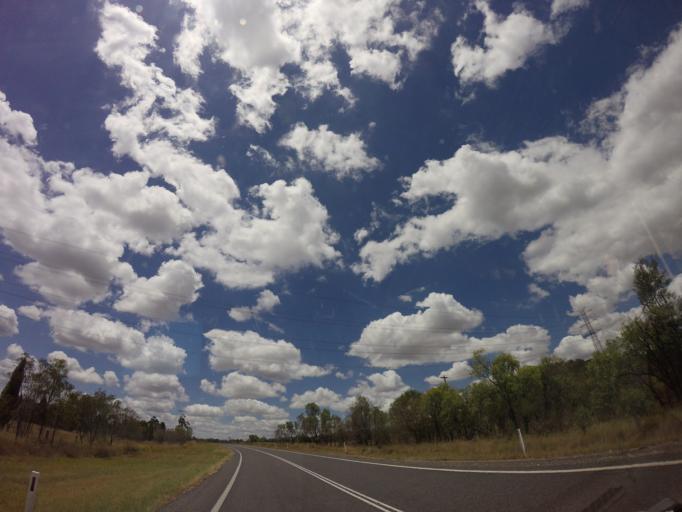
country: AU
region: Queensland
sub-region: Toowoomba
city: Oakey
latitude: -27.9338
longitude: 151.1687
